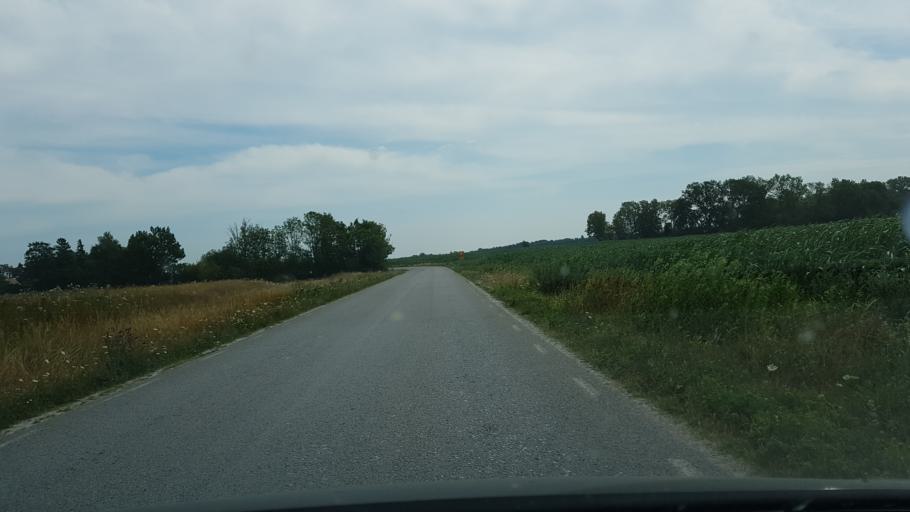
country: SE
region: Gotland
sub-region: Gotland
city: Visby
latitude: 57.7065
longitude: 18.5077
